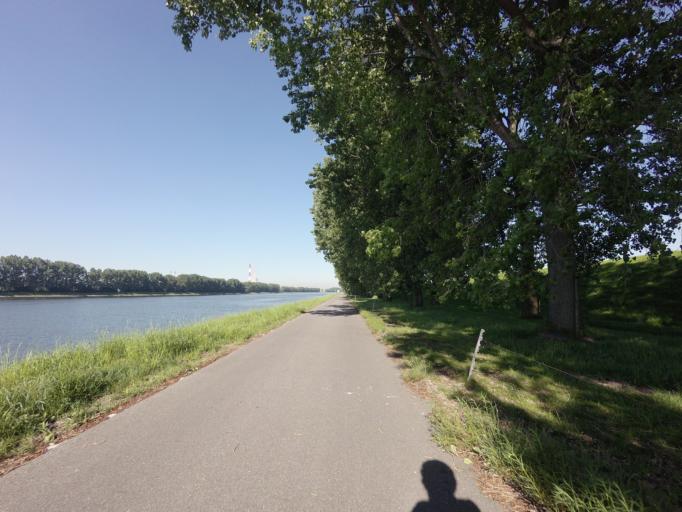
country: NL
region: North Brabant
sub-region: Gemeente Woensdrecht
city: Woensdrecht
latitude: 51.3743
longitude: 4.2934
